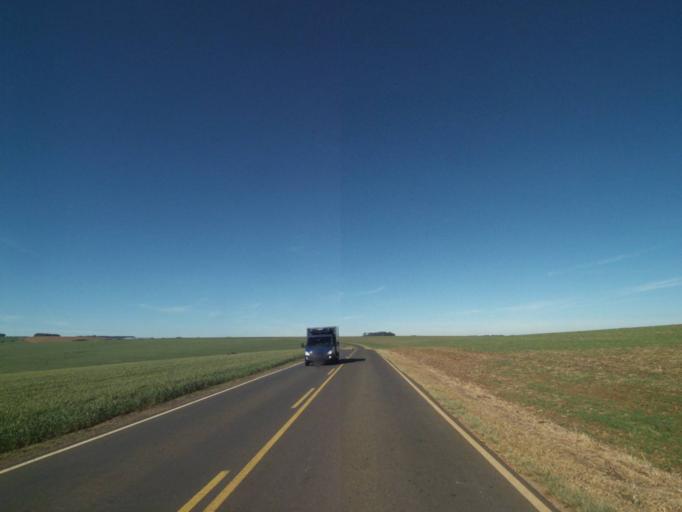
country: BR
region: Parana
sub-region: Tibagi
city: Tibagi
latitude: -24.5598
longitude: -50.2905
